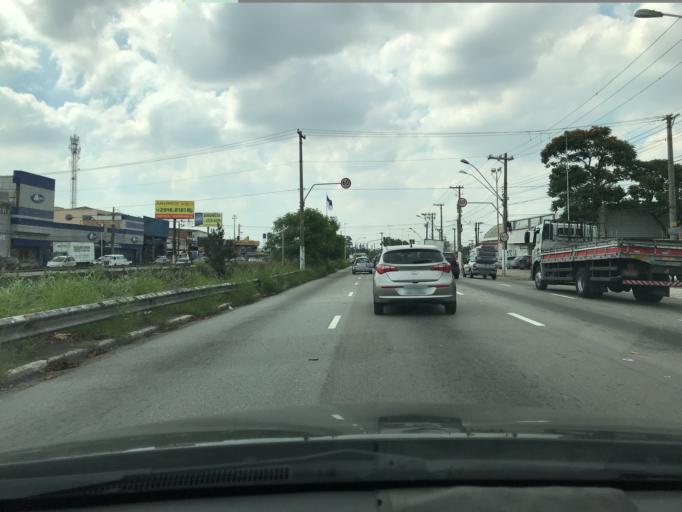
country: BR
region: Sao Paulo
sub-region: Sao Caetano Do Sul
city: Sao Caetano do Sul
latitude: -23.6260
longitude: -46.5404
